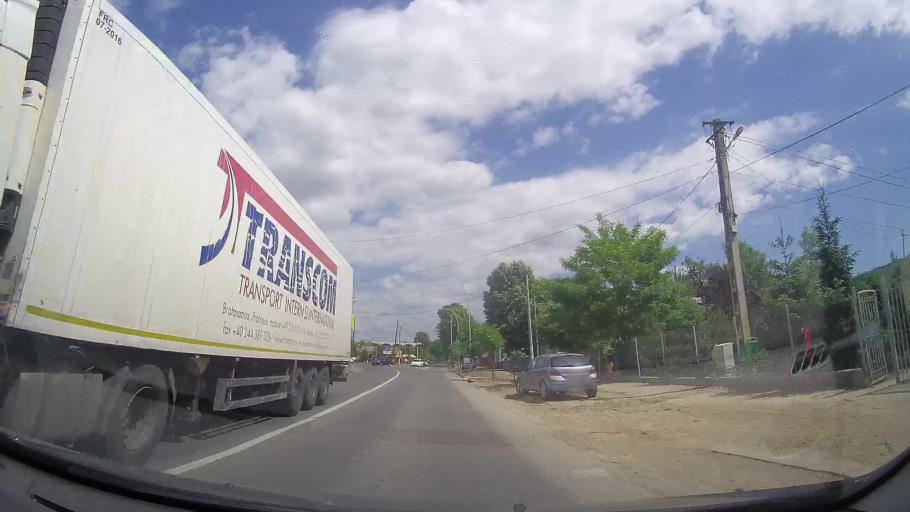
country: RO
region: Prahova
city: Drajna de Jos
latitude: 45.1993
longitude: 26.0438
